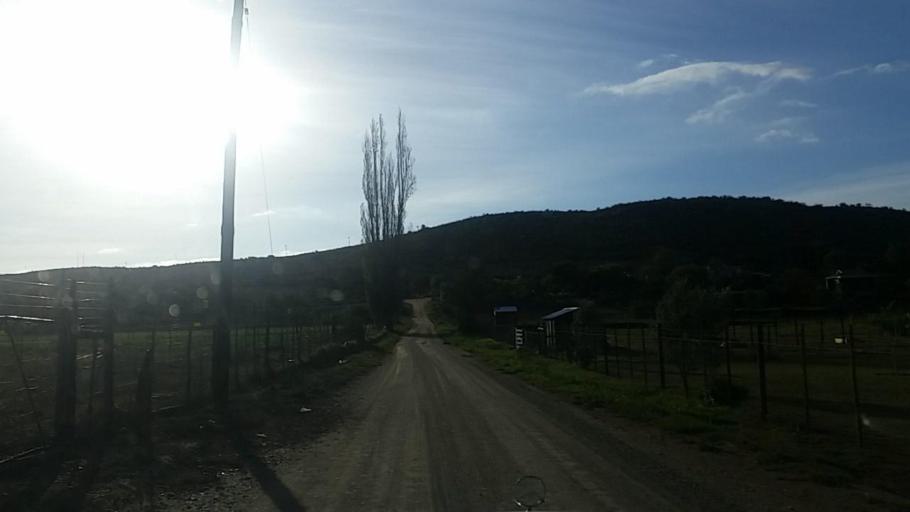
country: ZA
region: Western Cape
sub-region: Eden District Municipality
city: Knysna
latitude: -33.6572
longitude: 23.1209
